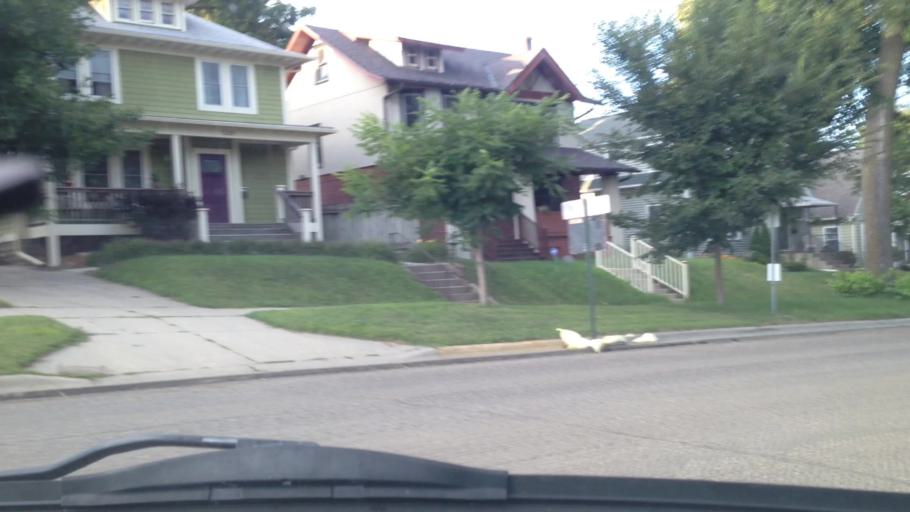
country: US
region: Minnesota
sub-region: Olmsted County
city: Rochester
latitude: 44.0170
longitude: -92.4713
